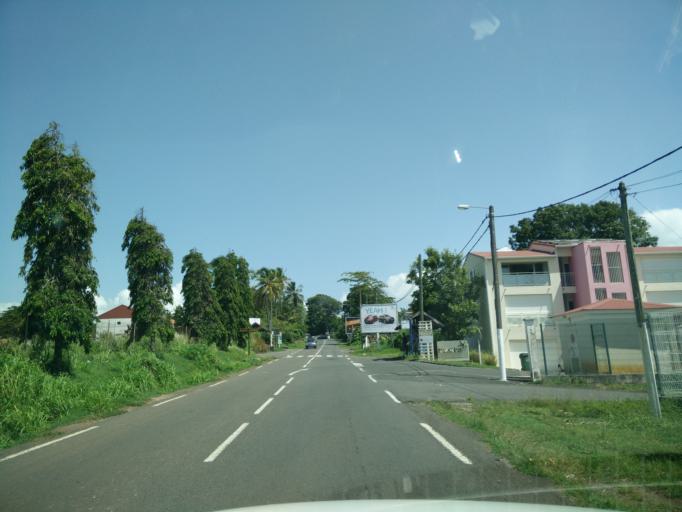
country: GP
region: Guadeloupe
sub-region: Guadeloupe
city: Petit-Bourg
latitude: 16.1822
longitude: -61.5880
